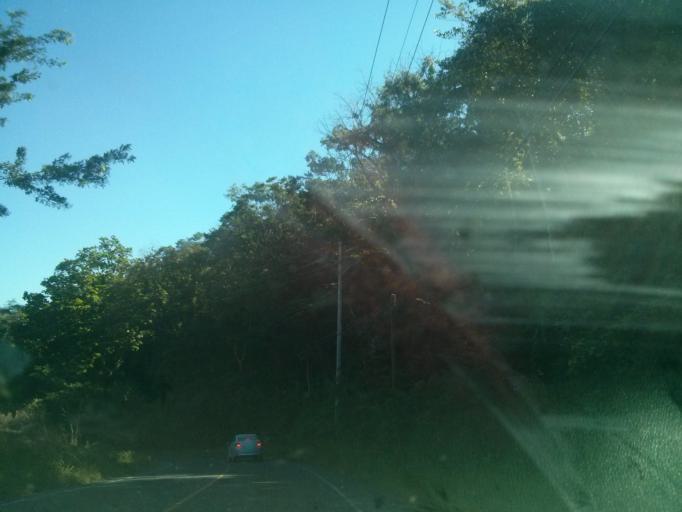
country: CR
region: Puntarenas
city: Paquera
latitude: 9.7096
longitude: -85.0166
